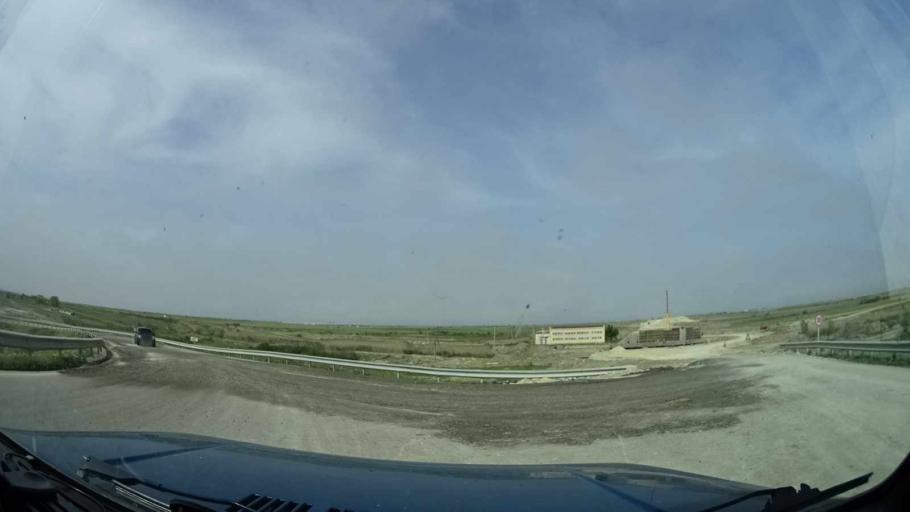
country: AZ
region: Xizi
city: Kilyazi
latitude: 40.8698
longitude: 49.3548
